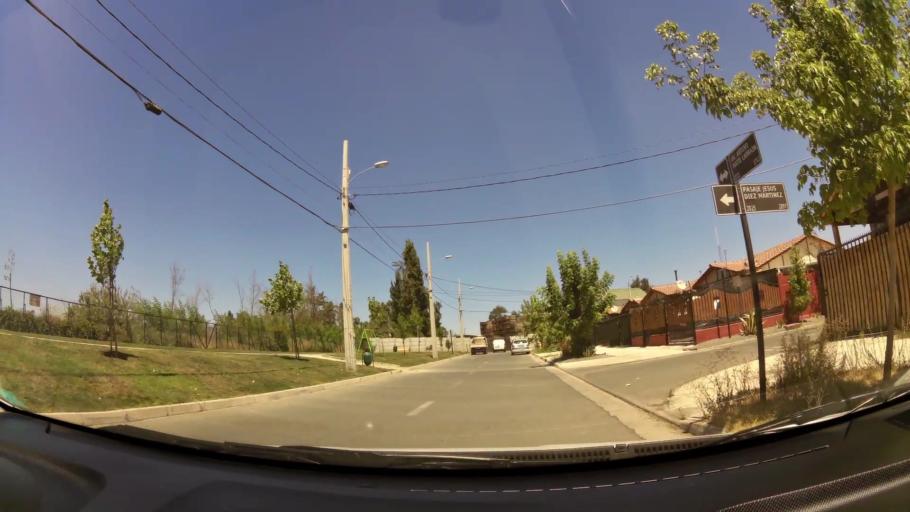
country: CL
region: O'Higgins
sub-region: Provincia de Cachapoal
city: Rancagua
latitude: -34.1535
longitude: -70.7614
